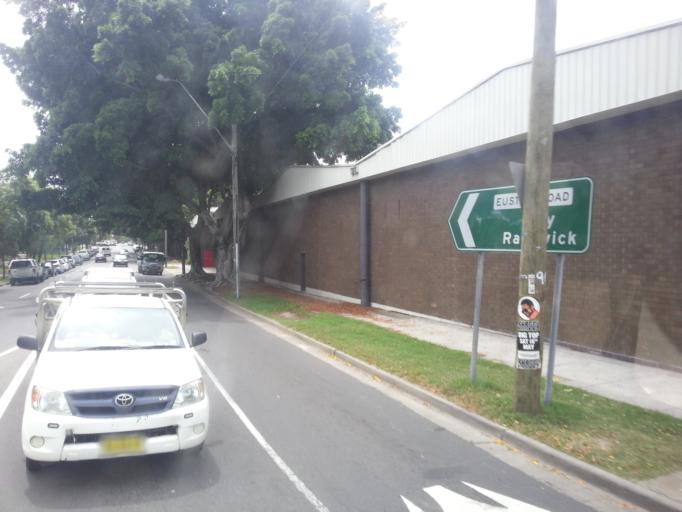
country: AU
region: New South Wales
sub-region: City of Sydney
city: Alexandria
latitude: -33.9077
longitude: 151.1903
